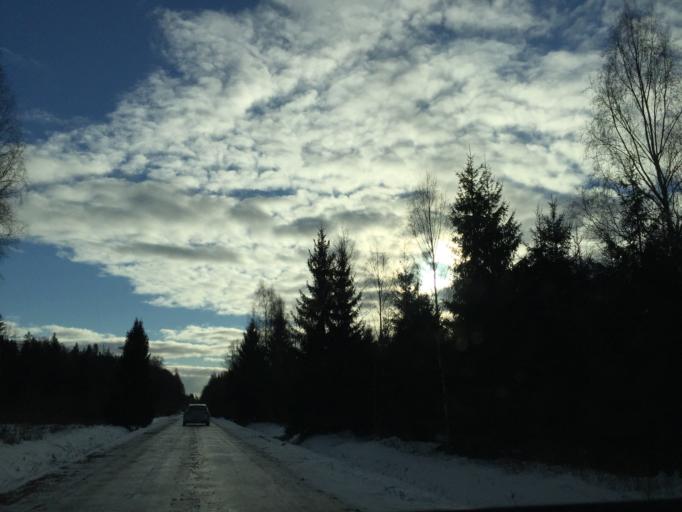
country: LV
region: Ogre
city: Jumprava
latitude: 56.5555
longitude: 24.8565
